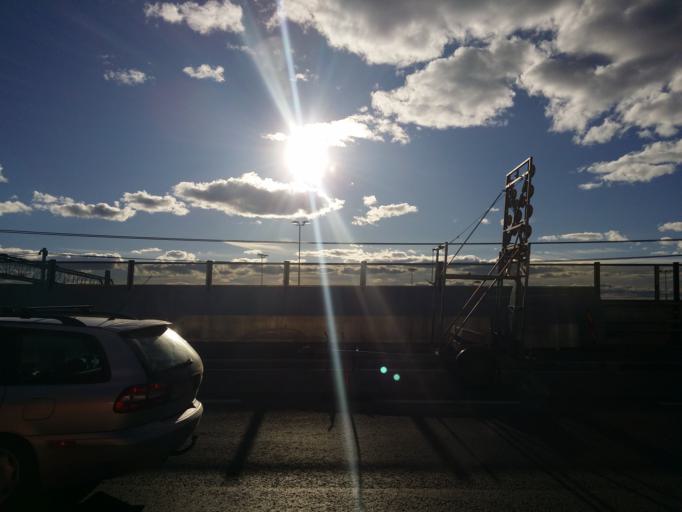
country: NO
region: Oslo
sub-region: Oslo
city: Oslo
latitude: 59.8971
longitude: 10.7561
